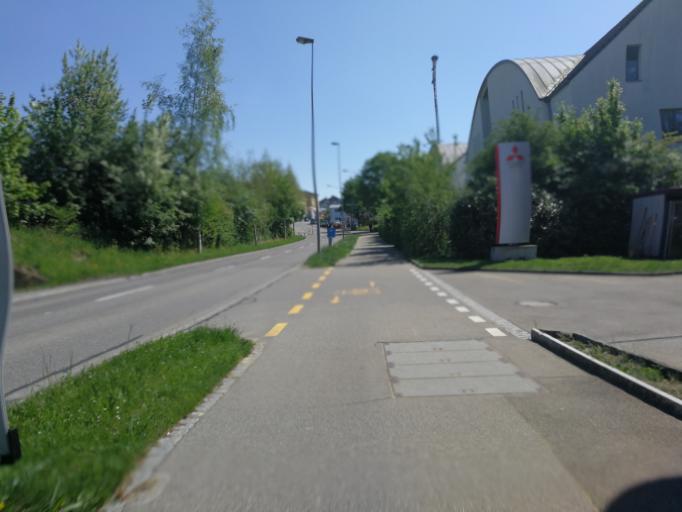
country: CH
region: Zurich
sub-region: Bezirk Meilen
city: Oetwil am See
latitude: 47.2751
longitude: 8.7192
